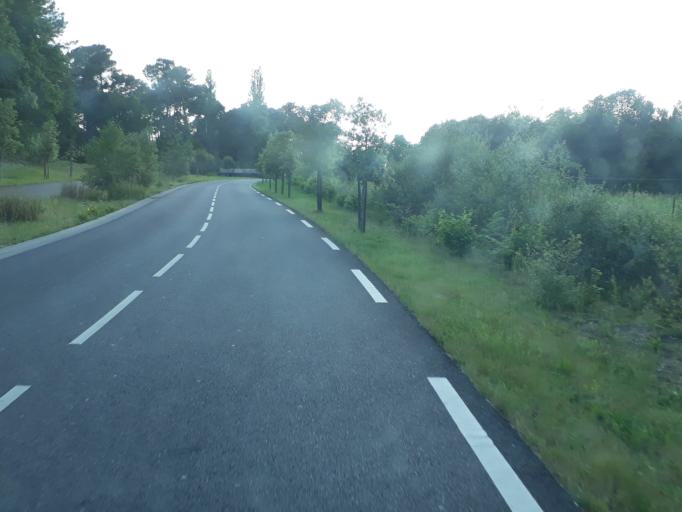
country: FR
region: Aquitaine
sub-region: Departement des Landes
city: Mont-de-Marsan
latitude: 43.9048
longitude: -0.4892
